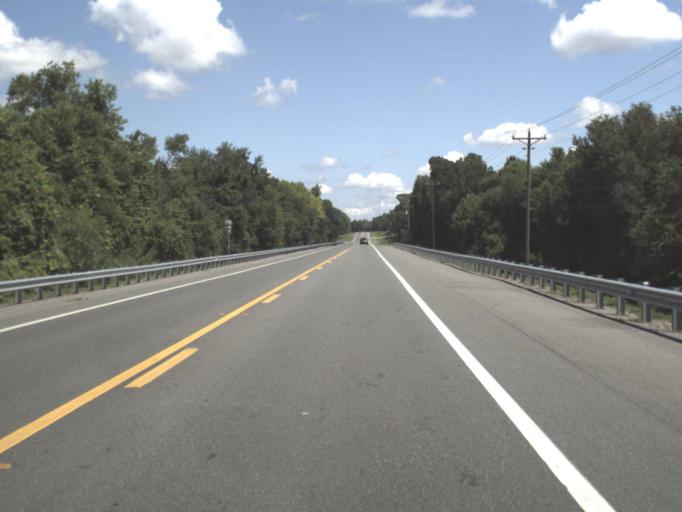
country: US
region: Florida
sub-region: Clay County
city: Keystone Heights
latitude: 29.7495
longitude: -81.9939
